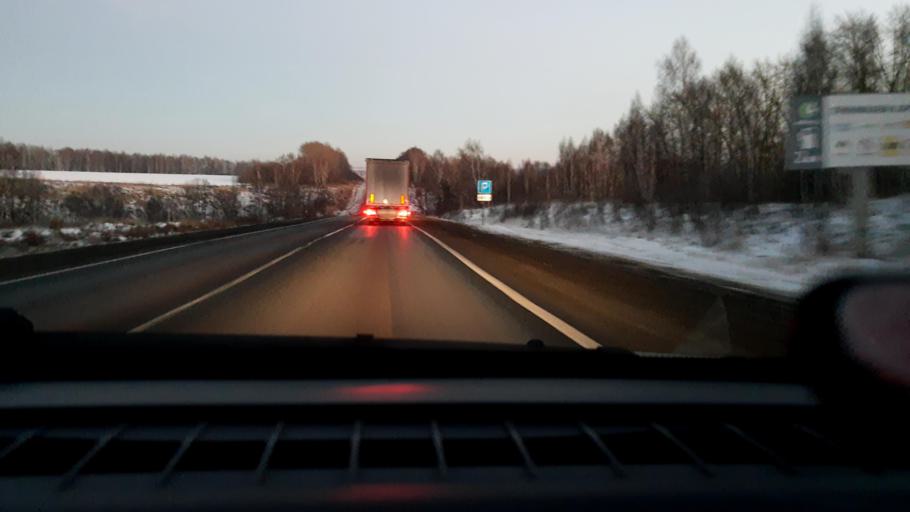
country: RU
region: Nizjnij Novgorod
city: Lyskovo
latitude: 56.0080
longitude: 44.8750
